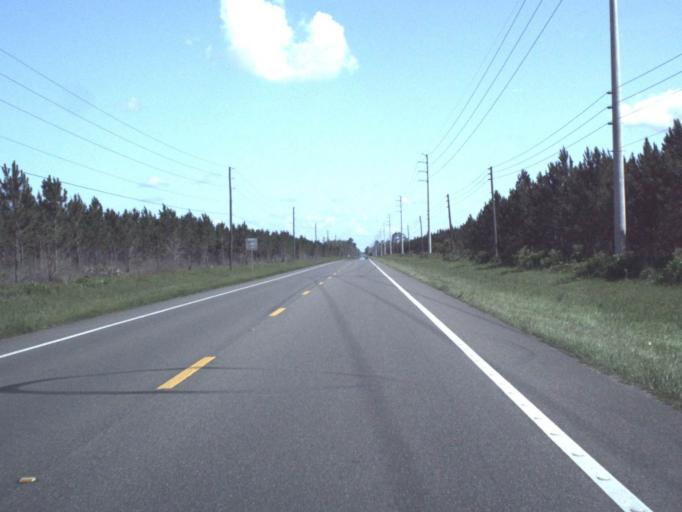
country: US
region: Florida
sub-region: Bradford County
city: Starke
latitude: 29.8719
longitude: -82.0777
